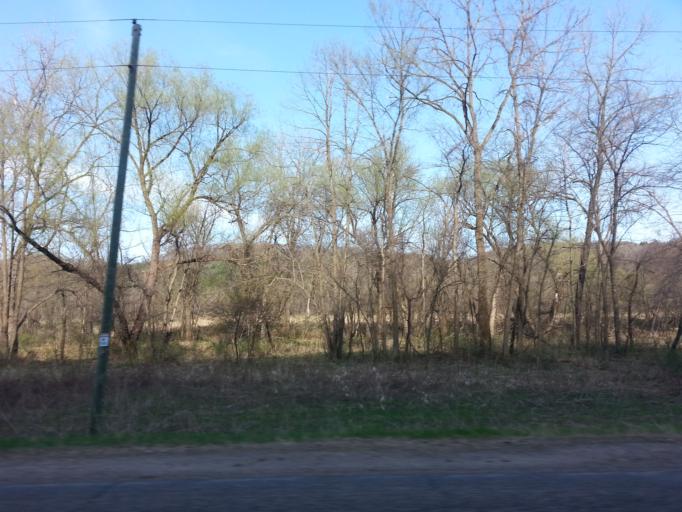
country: US
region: Minnesota
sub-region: Goodhue County
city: Red Wing
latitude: 44.6547
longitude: -92.5912
